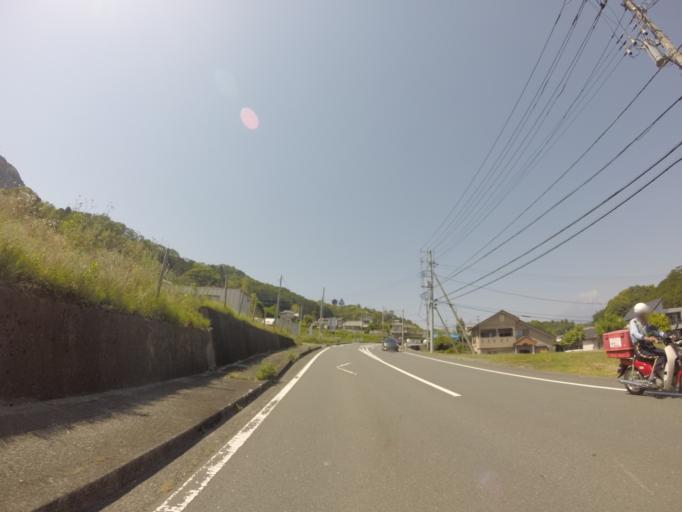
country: JP
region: Shizuoka
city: Fujinomiya
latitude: 35.2097
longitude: 138.5866
